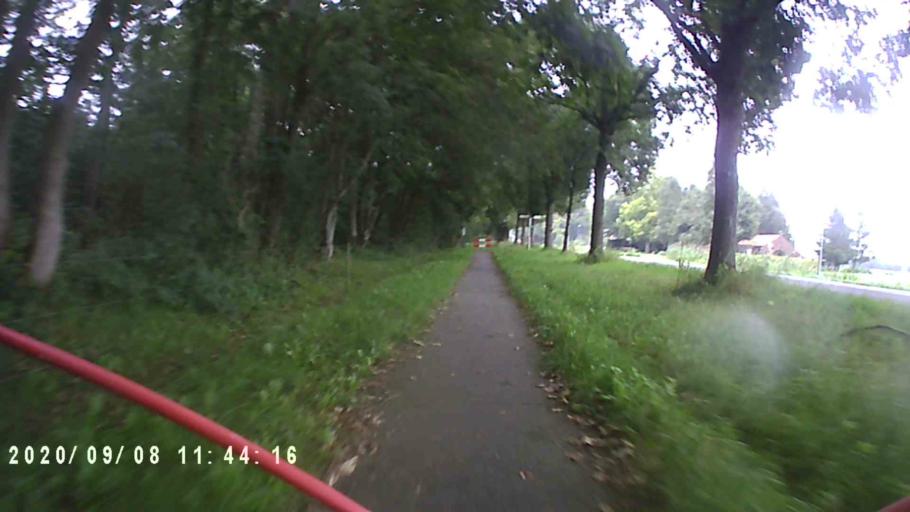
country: NL
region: Groningen
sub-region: Gemeente Hoogezand-Sappemeer
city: Sappemeer
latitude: 53.1504
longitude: 6.7967
